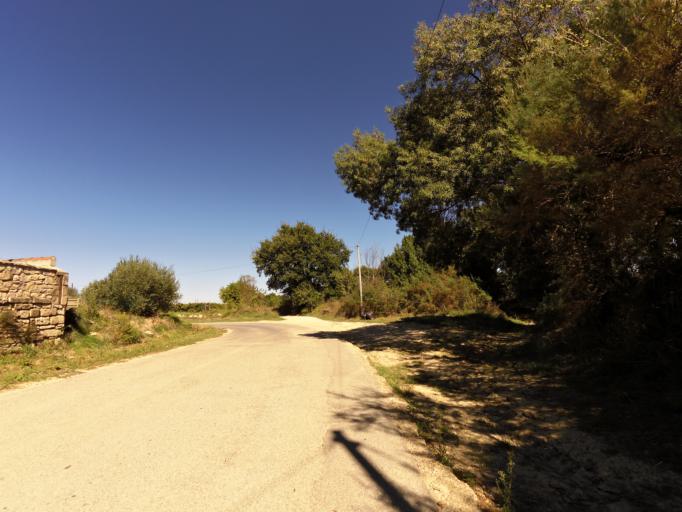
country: FR
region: Languedoc-Roussillon
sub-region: Departement du Gard
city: Codognan
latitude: 43.7344
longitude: 4.2152
